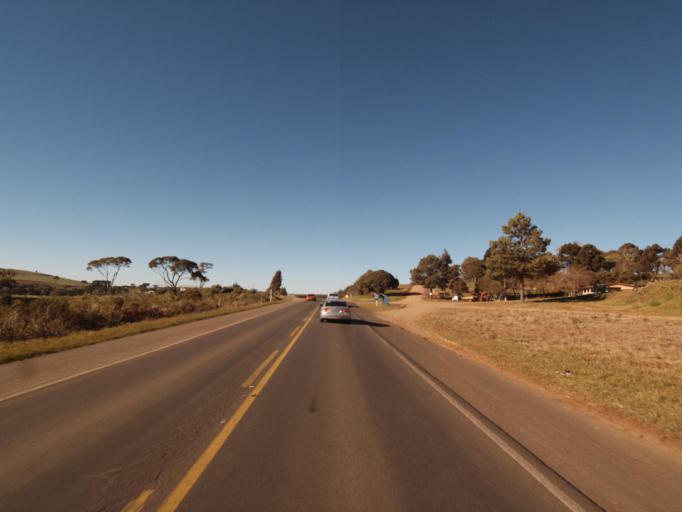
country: BR
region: Santa Catarina
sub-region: Concordia
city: Concordia
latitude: -26.9051
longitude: -51.9709
